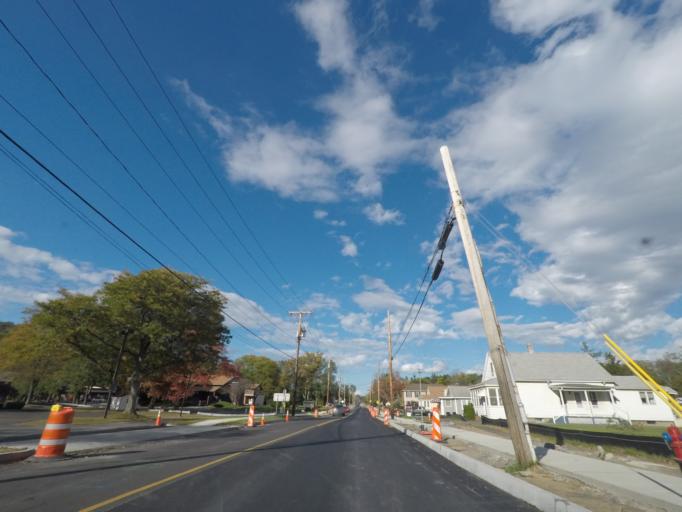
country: US
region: New York
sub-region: Schenectady County
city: Rotterdam
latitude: 42.7656
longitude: -73.9385
